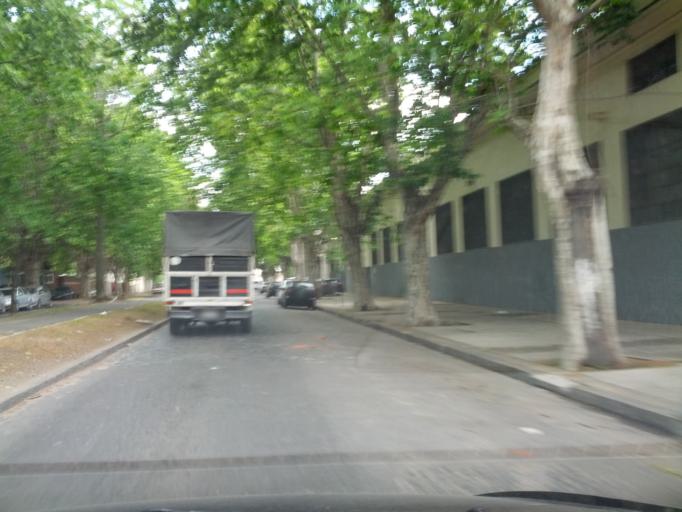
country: AR
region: Buenos Aires
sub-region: Partido de Lanus
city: Lanus
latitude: -34.6588
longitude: -58.4217
